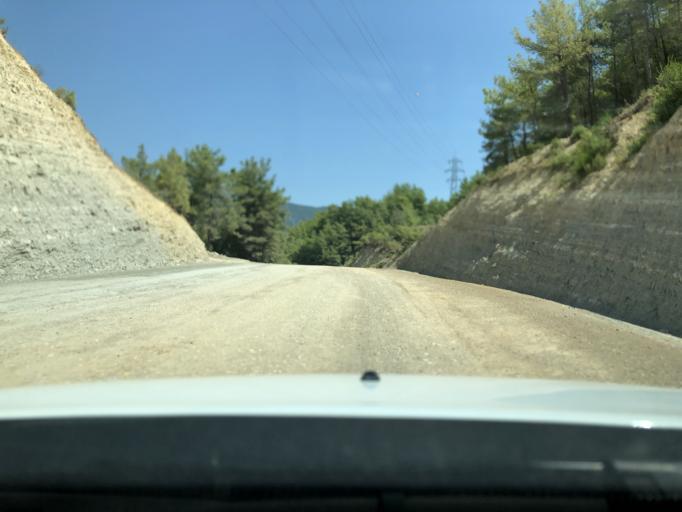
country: TR
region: Antalya
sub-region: Manavgat
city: Manavgat
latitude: 36.8361
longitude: 31.5350
